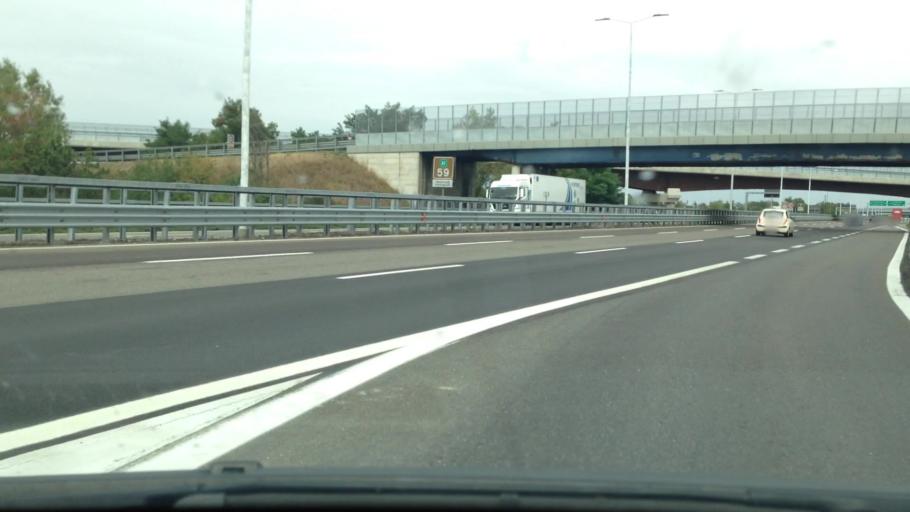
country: IT
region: Piedmont
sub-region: Provincia di Alessandria
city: Tortona
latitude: 44.9079
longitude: 8.8438
